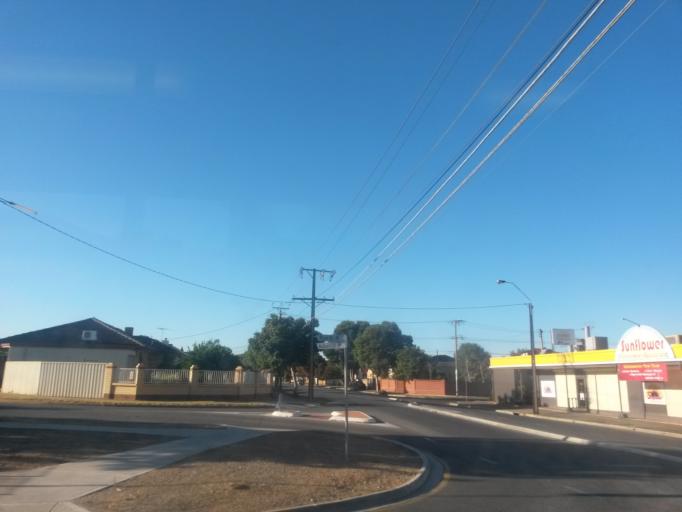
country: AU
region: South Australia
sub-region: Charles Sturt
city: Woodville
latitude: -34.8826
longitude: 138.5669
